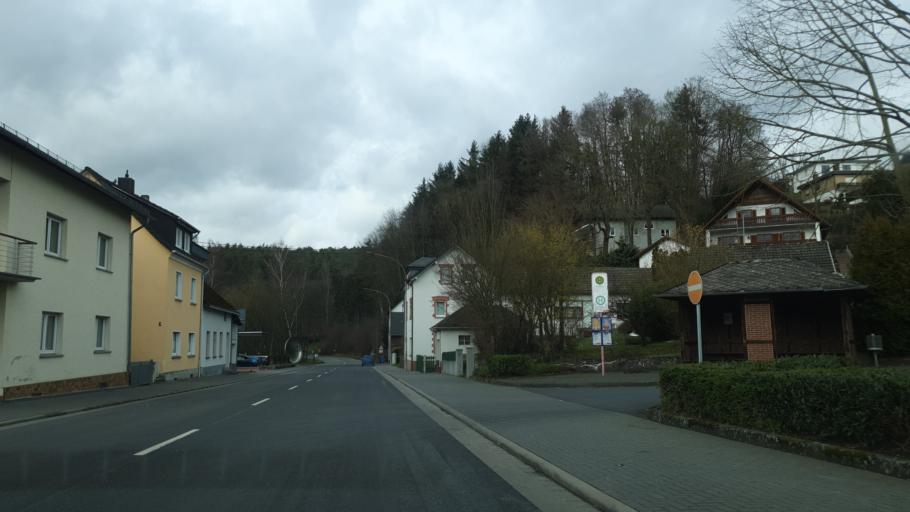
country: DE
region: Rheinland-Pfalz
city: Puderbach
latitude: 50.6005
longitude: 7.6112
